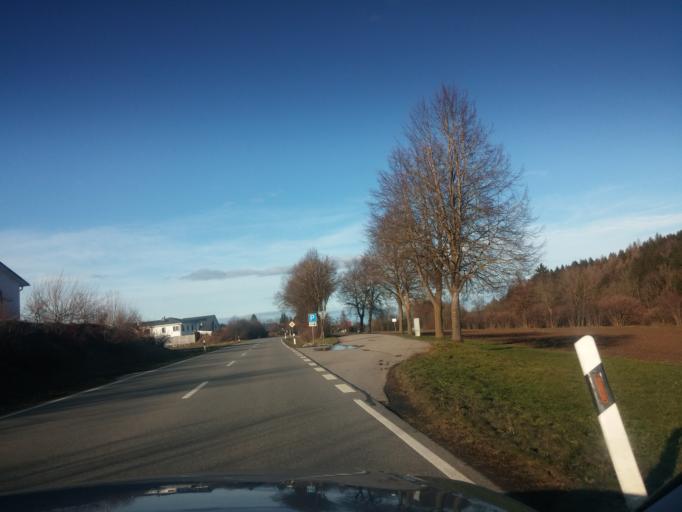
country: DE
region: Bavaria
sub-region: Swabia
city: Lautrach
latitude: 47.8928
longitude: 10.1209
